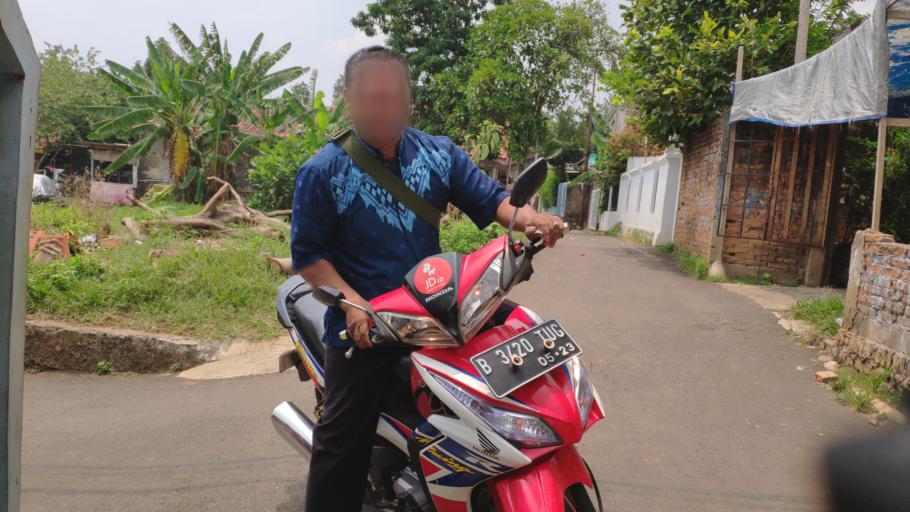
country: ID
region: West Java
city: Depok
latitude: -6.3176
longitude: 106.8296
